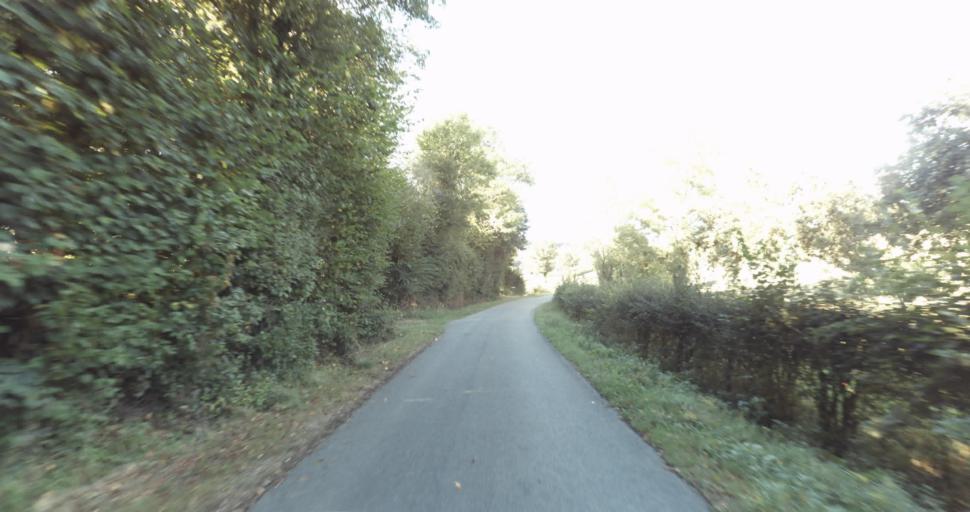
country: FR
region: Lower Normandy
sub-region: Departement de l'Orne
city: Vimoutiers
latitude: 48.9069
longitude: 0.1212
